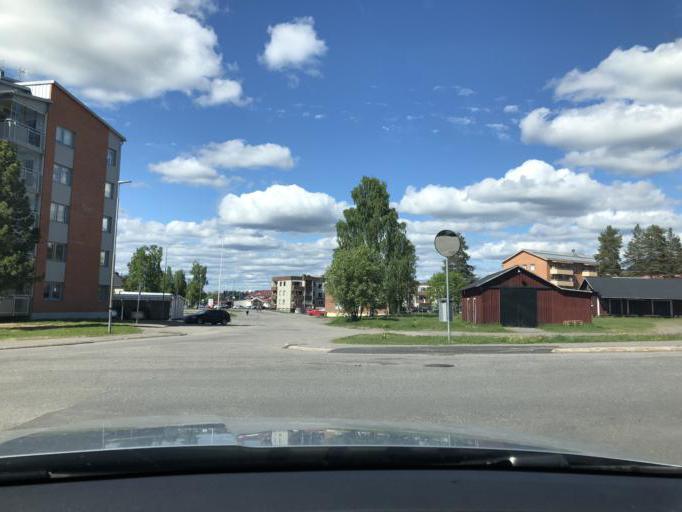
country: SE
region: Norrbotten
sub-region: Alvsbyns Kommun
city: AElvsbyn
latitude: 65.6704
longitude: 21.0123
